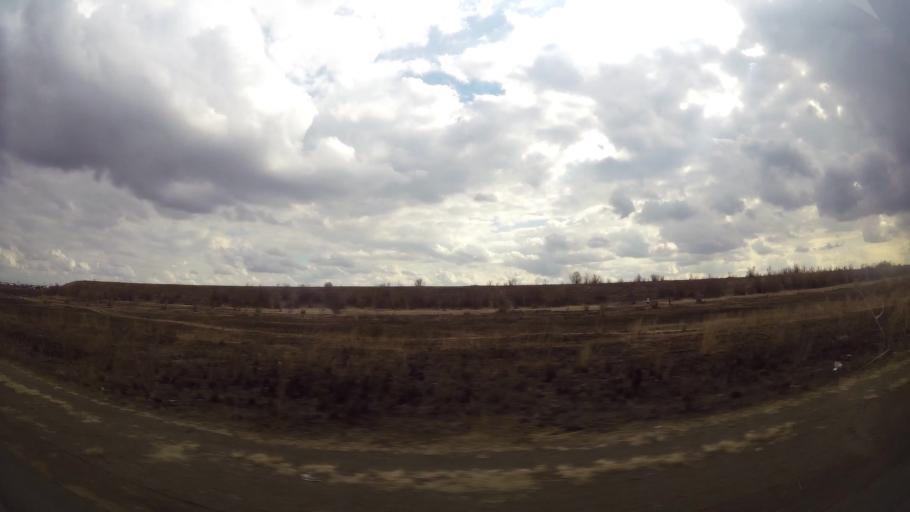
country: ZA
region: Orange Free State
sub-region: Fezile Dabi District Municipality
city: Sasolburg
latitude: -26.8771
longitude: 27.8867
